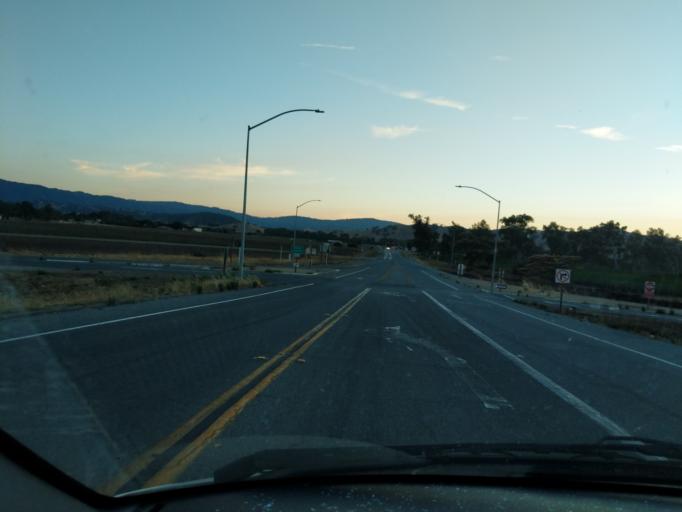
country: US
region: California
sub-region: Santa Clara County
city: San Martin
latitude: 37.0588
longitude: -121.5864
